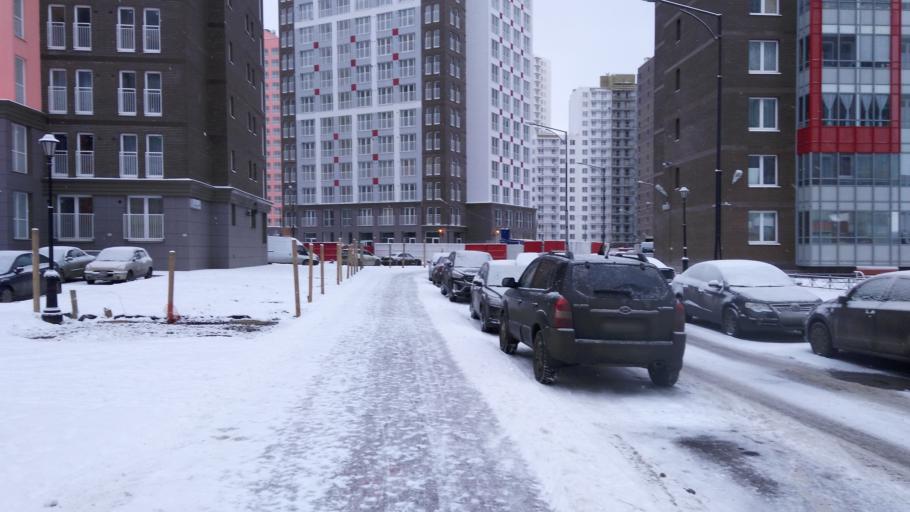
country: RU
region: Leningrad
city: Rybatskoye
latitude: 59.8985
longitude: 30.5152
